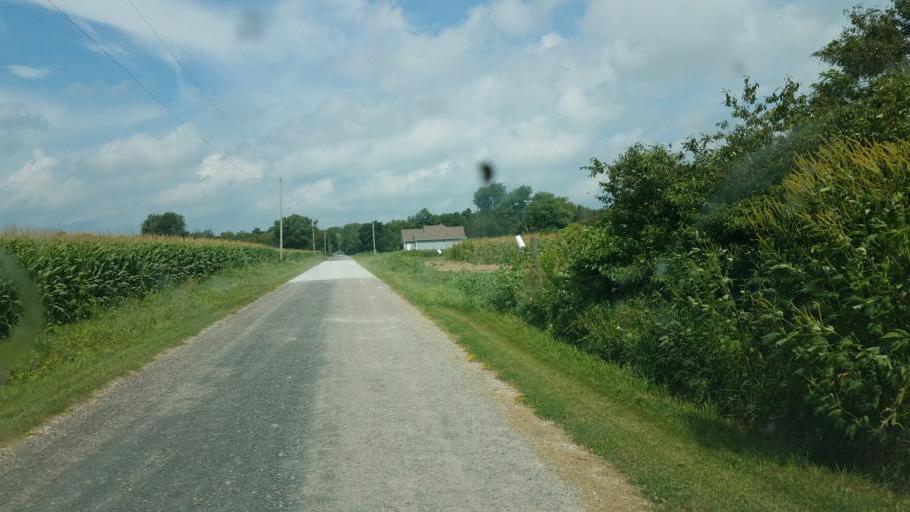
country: US
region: Ohio
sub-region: Morrow County
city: Mount Gilead
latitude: 40.6121
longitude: -82.7092
